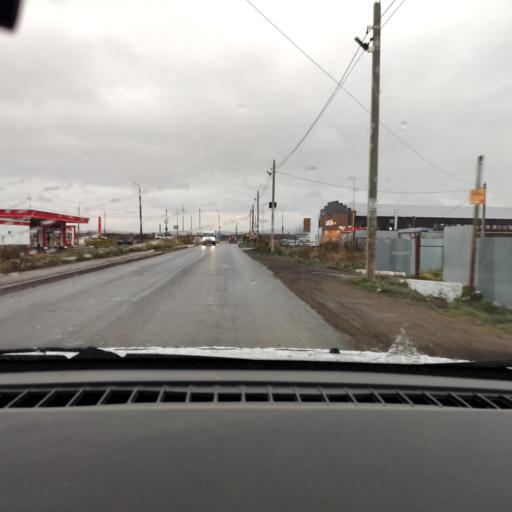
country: RU
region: Perm
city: Kultayevo
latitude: 57.8980
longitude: 55.9627
